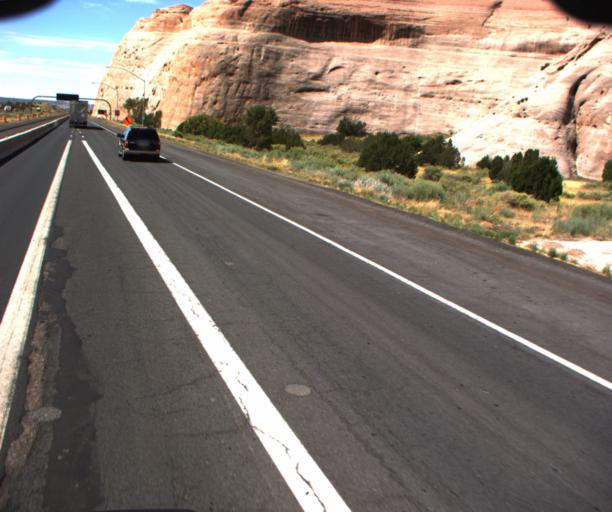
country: US
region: Arizona
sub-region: Apache County
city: Houck
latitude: 35.3505
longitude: -109.0585
